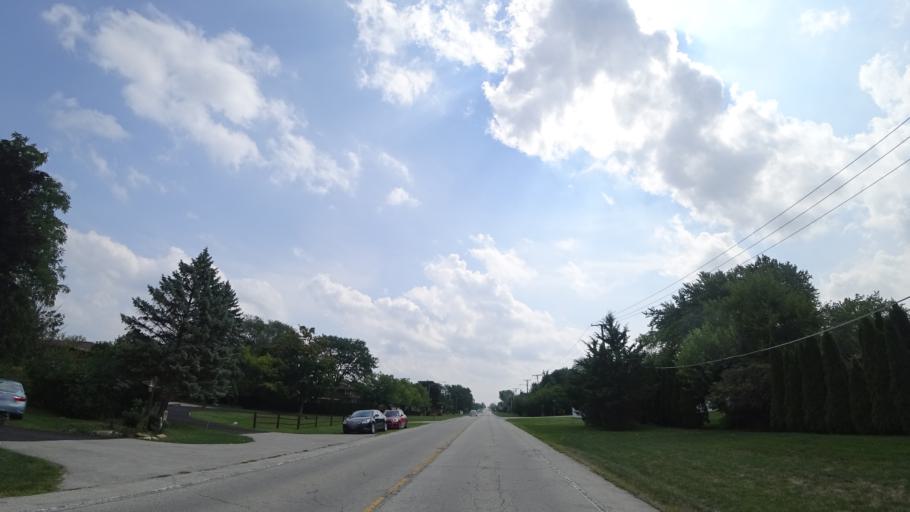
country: US
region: Illinois
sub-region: Will County
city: Goodings Grove
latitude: 41.6356
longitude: -87.9117
